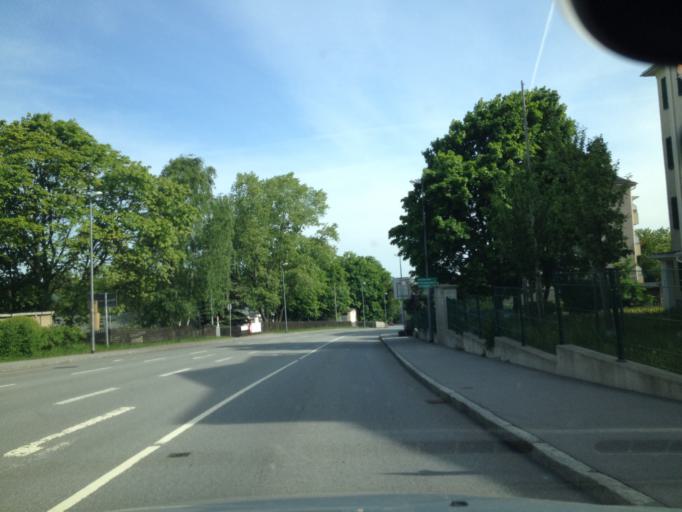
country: DE
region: Saxony
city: Annaberg-Buchholz
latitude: 50.5830
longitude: 13.0146
